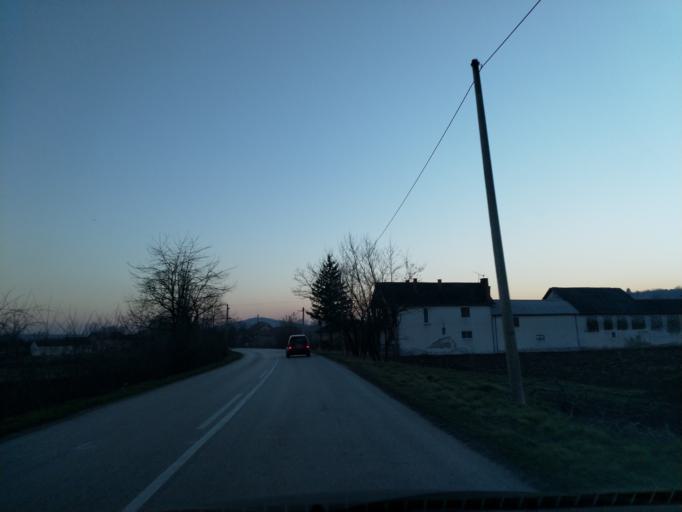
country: RS
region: Central Serbia
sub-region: Pomoravski Okrug
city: Paracin
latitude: 43.8904
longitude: 21.4835
